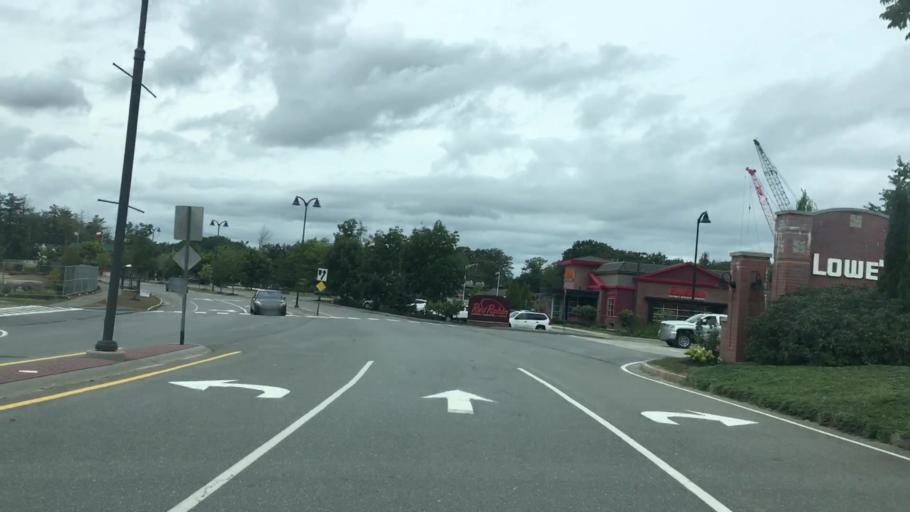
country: US
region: Maine
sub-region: Cumberland County
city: South Portland Gardens
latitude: 43.6240
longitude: -70.3400
